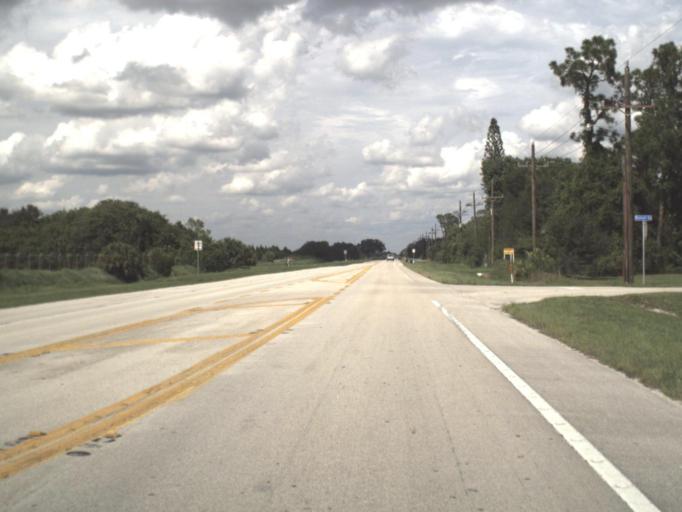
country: US
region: Florida
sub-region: Hendry County
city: LaBelle
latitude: 26.6762
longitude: -81.4365
